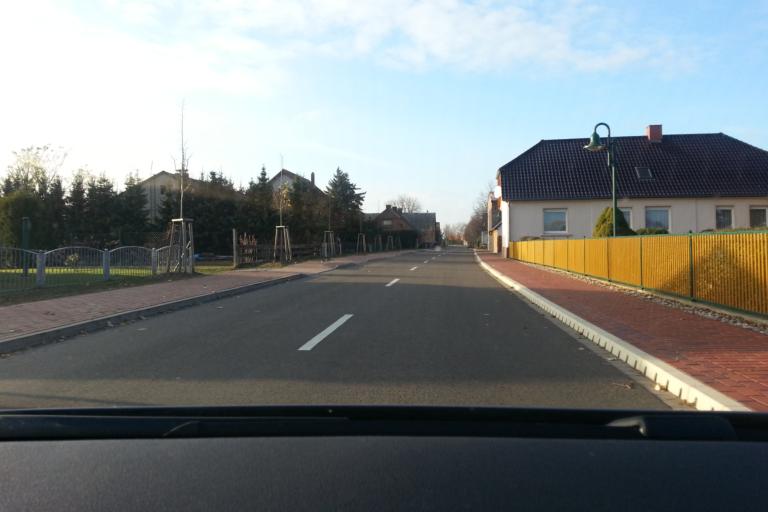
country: DE
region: Mecklenburg-Vorpommern
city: Strasburg
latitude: 53.6150
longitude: 13.7735
